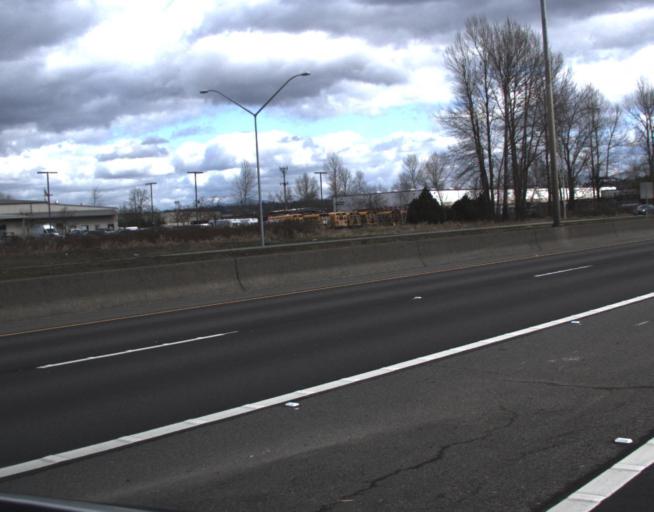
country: US
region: Washington
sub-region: King County
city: Lakeland South
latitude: 47.2896
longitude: -122.3107
